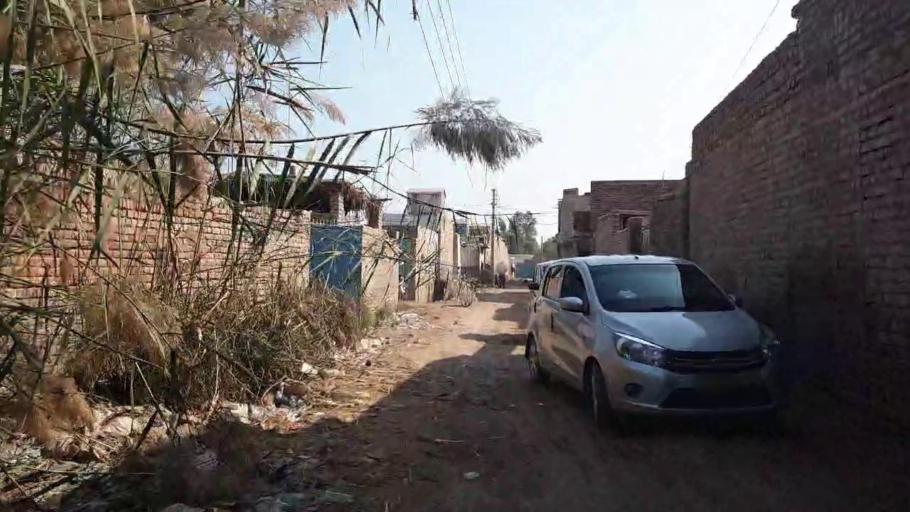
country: PK
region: Sindh
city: Hala
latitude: 25.8901
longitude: 68.4136
